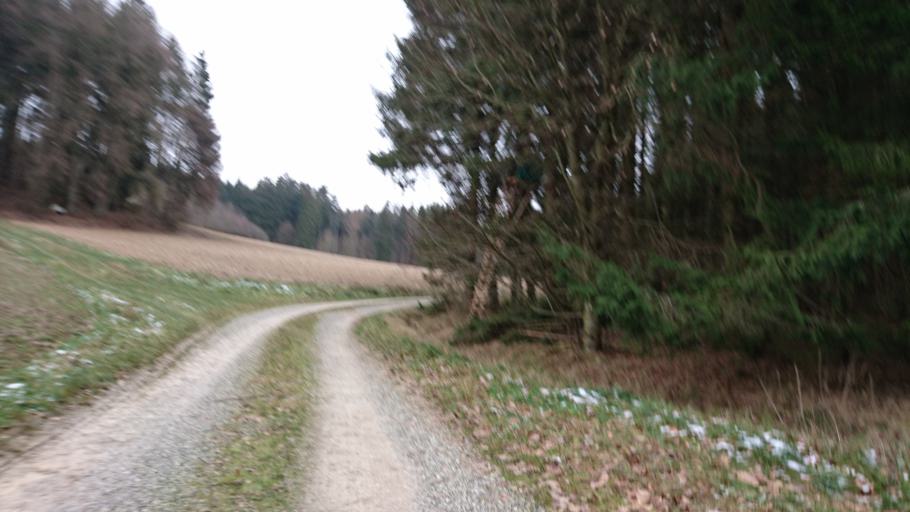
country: DE
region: Bavaria
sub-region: Swabia
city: Zusmarshausen
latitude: 48.4302
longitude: 10.6173
